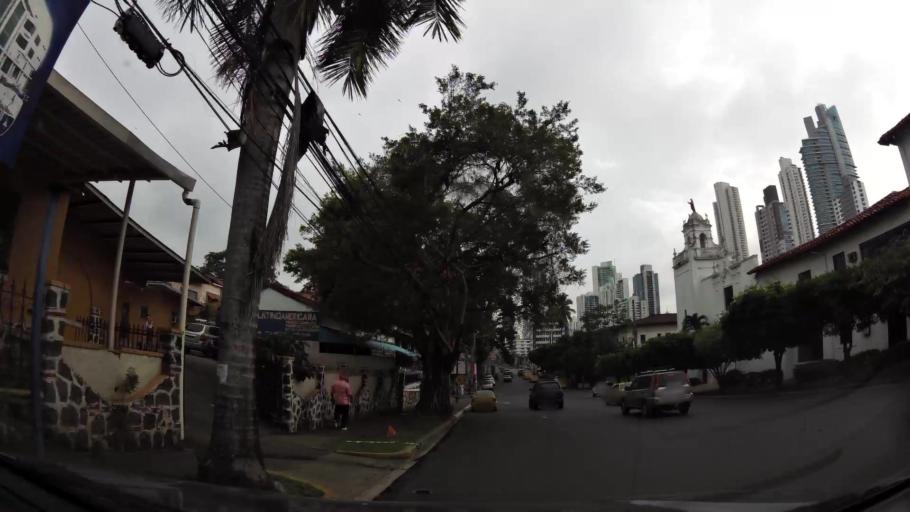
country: PA
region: Panama
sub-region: Distrito de Panama
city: Ancon
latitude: 8.9710
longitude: -79.5339
